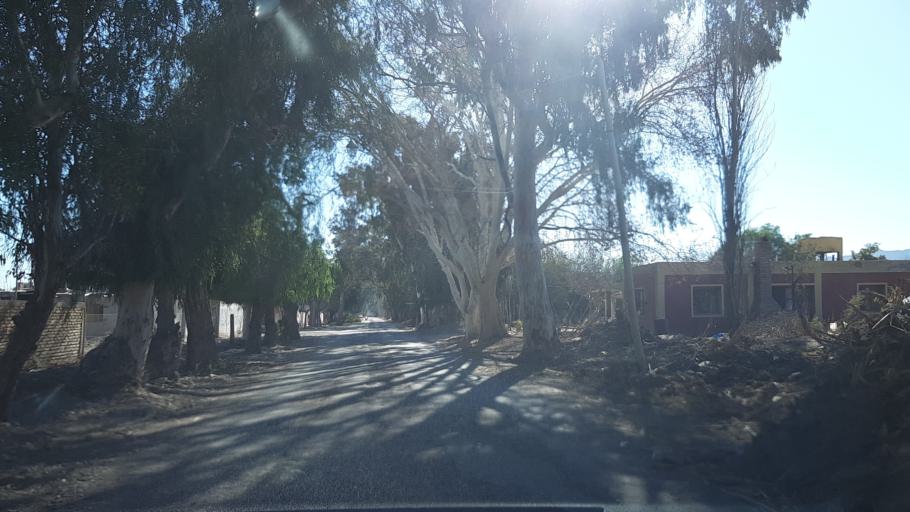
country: AR
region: San Juan
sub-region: Departamento de Zonda
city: Zonda
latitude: -31.5506
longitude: -68.7275
